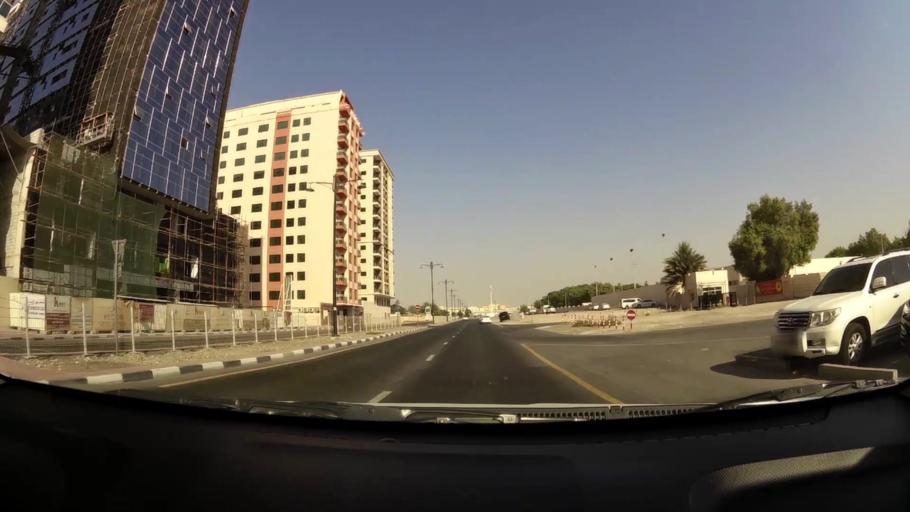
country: AE
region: Ash Shariqah
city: Sharjah
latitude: 25.2882
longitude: 55.3769
